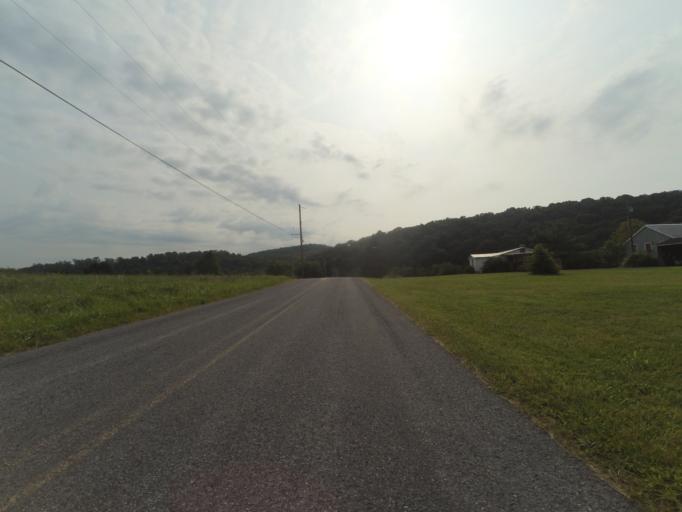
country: US
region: Pennsylvania
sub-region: Huntingdon County
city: McConnellstown
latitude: 40.5226
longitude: -78.0958
